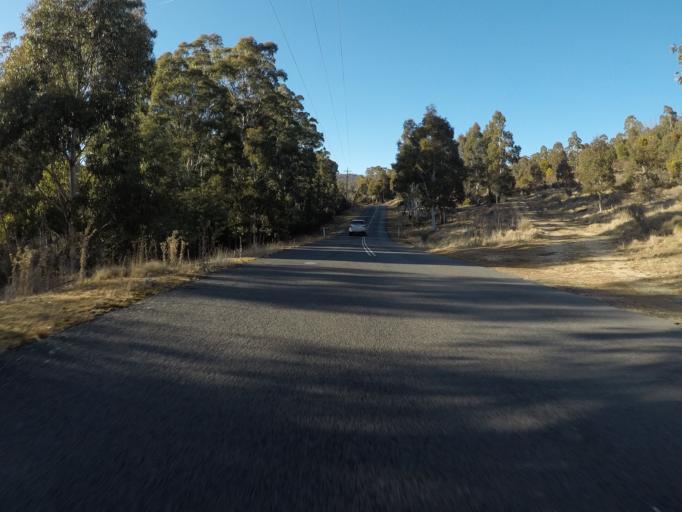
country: AU
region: Australian Capital Territory
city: Macarthur
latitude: -35.5063
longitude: 148.9253
